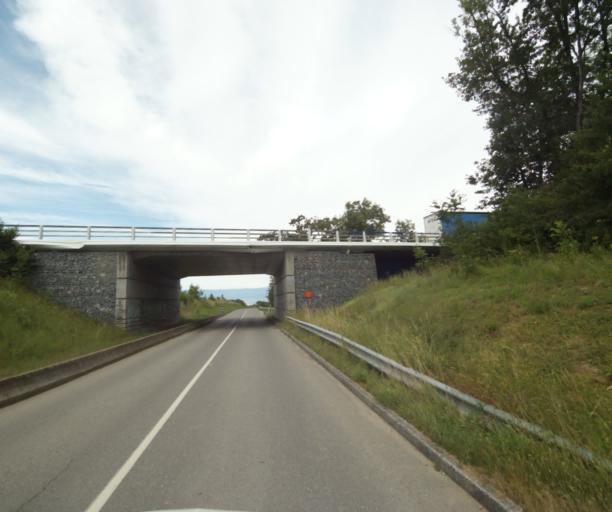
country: FR
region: Rhone-Alpes
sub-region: Departement de la Haute-Savoie
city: Allinges
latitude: 46.3468
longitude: 6.4533
